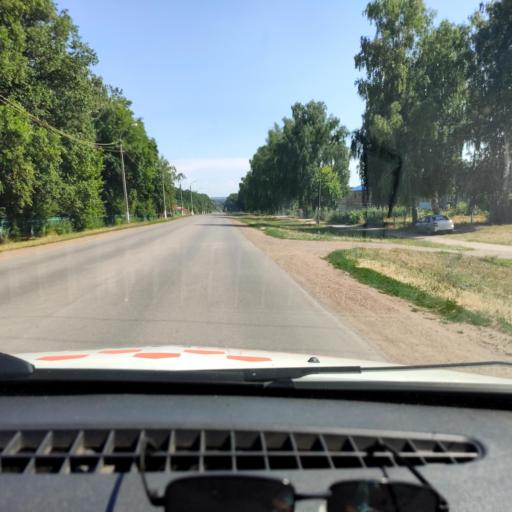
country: RU
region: Bashkortostan
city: Tolbazy
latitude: 54.0085
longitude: 55.8896
